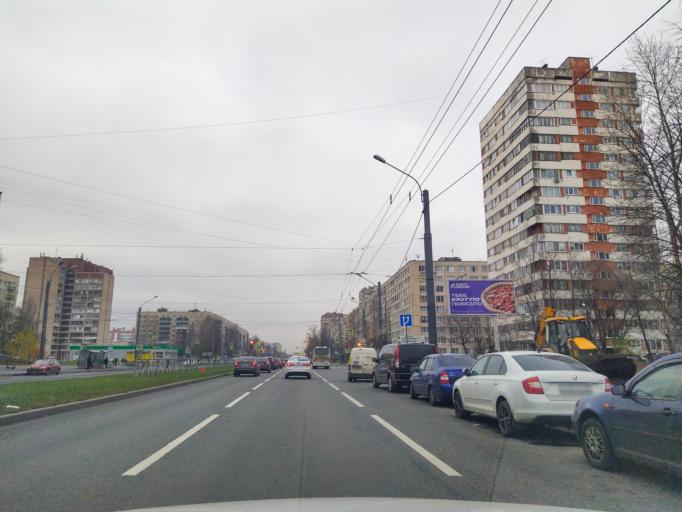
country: RU
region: St.-Petersburg
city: Sosnovka
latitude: 60.0423
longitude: 30.3490
